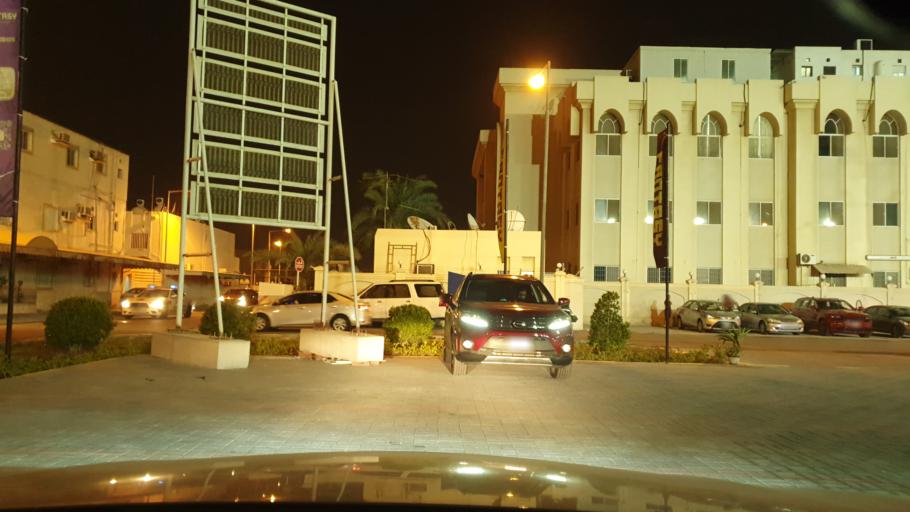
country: BH
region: Muharraq
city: Al Hadd
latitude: 26.2555
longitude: 50.6433
